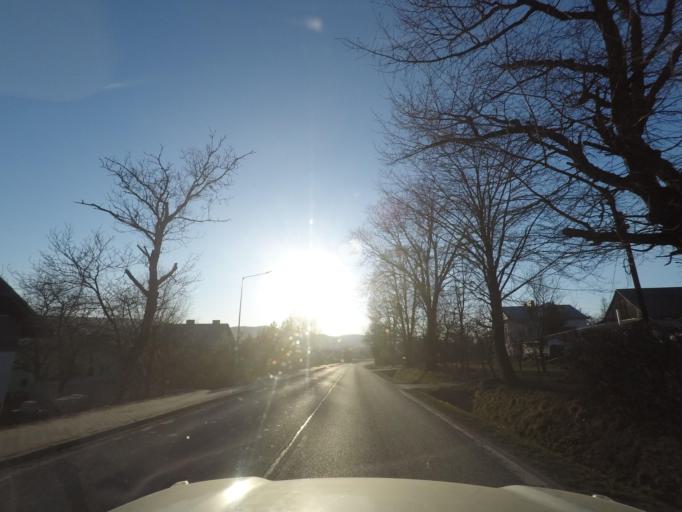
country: PL
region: Subcarpathian Voivodeship
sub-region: Powiat krosnienski
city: Dukla
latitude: 49.5576
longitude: 21.6475
